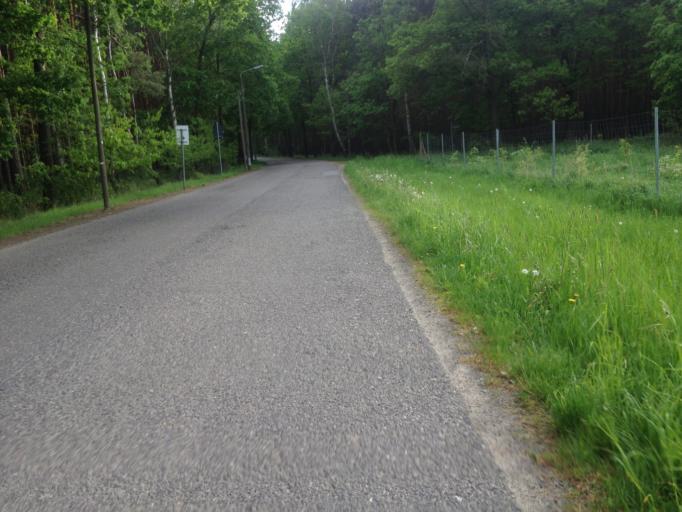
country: DE
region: Brandenburg
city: Cottbus
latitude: 51.8170
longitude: 14.3206
